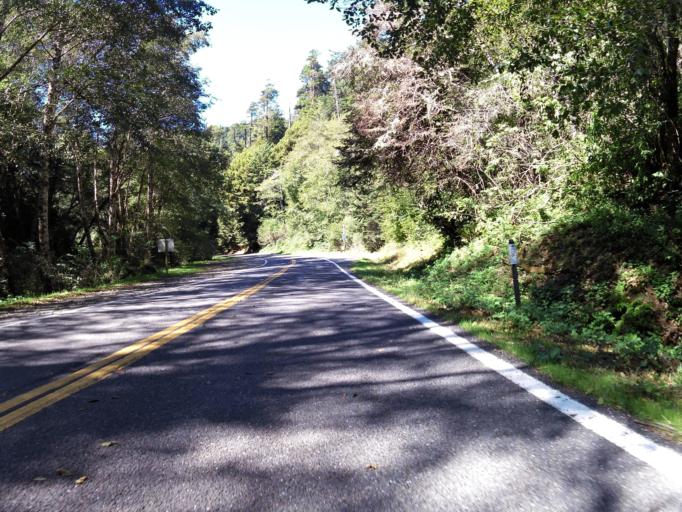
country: US
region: California
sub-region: Mendocino County
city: Fort Bragg
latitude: 39.7806
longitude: -123.8280
